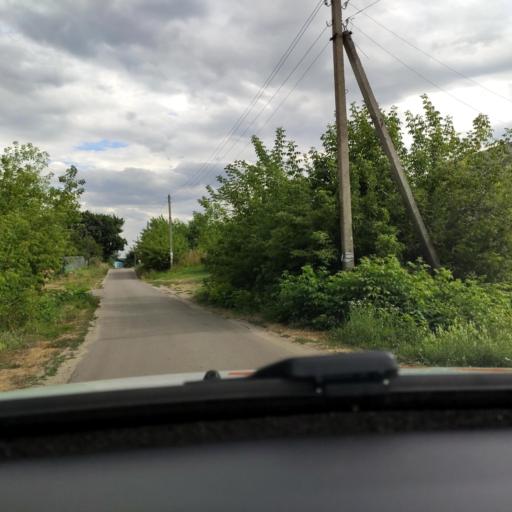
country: RU
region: Voronezj
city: Orlovo
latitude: 51.6497
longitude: 39.5701
